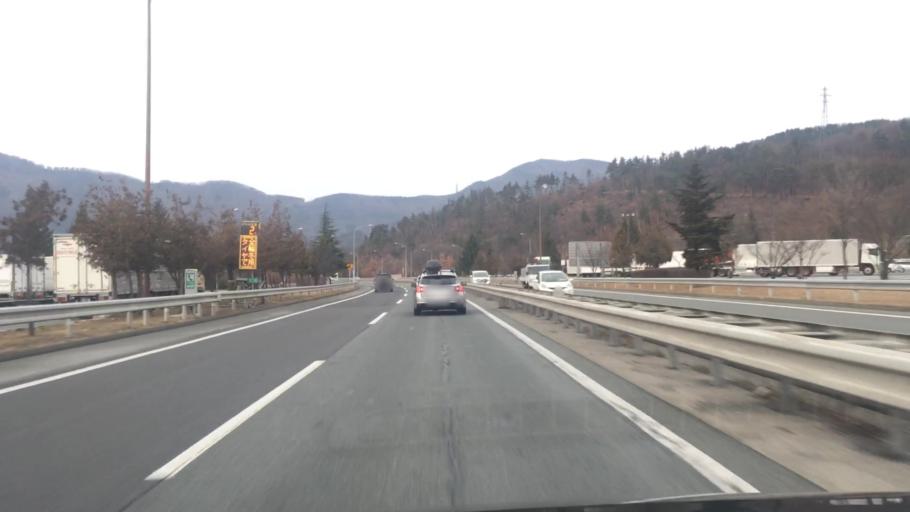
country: JP
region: Nagano
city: Ueda
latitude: 36.4553
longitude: 138.2005
